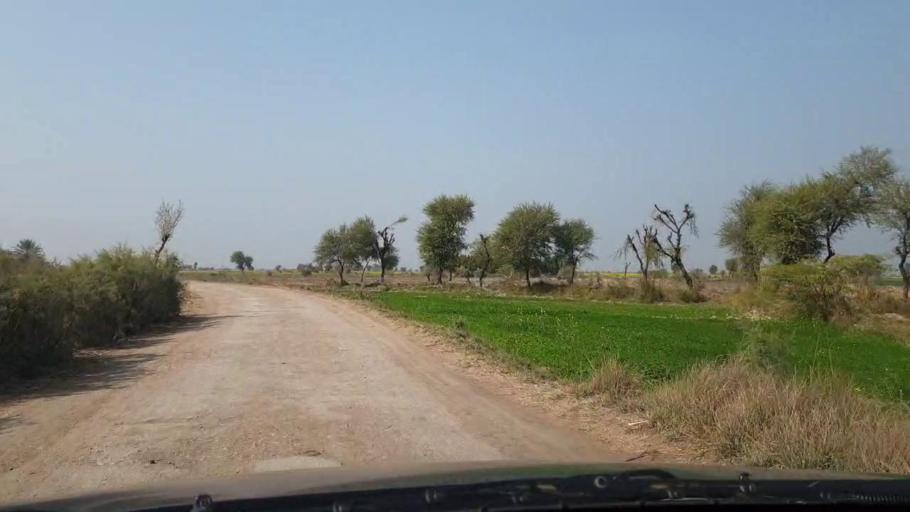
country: PK
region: Sindh
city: Sanghar
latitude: 26.0169
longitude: 68.9205
